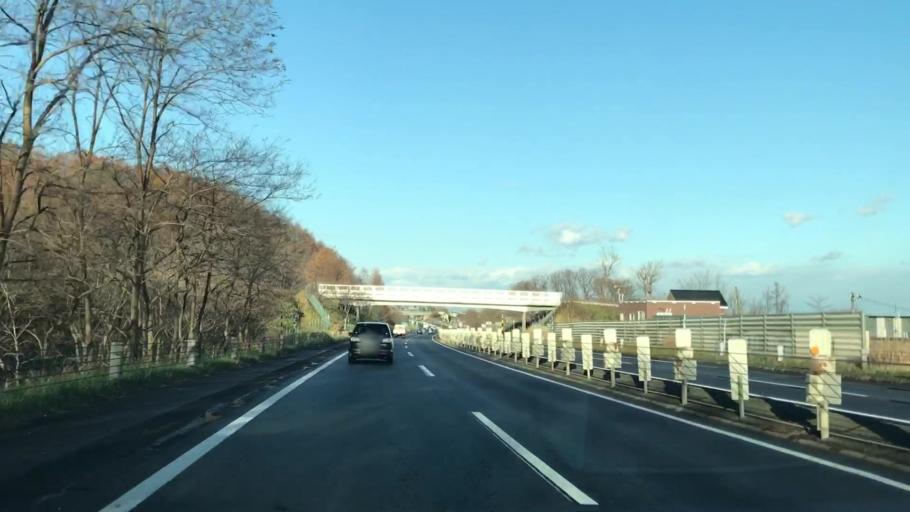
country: JP
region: Hokkaido
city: Sapporo
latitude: 43.1202
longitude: 141.2201
